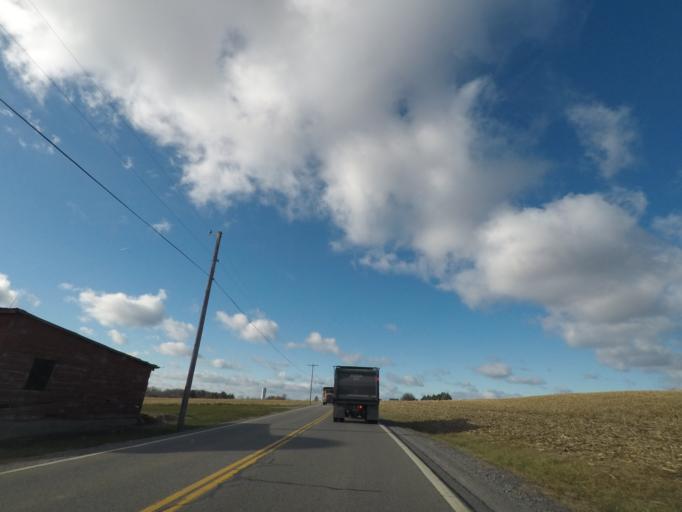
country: US
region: New York
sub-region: Saratoga County
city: Waterford
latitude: 42.8347
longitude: -73.6943
